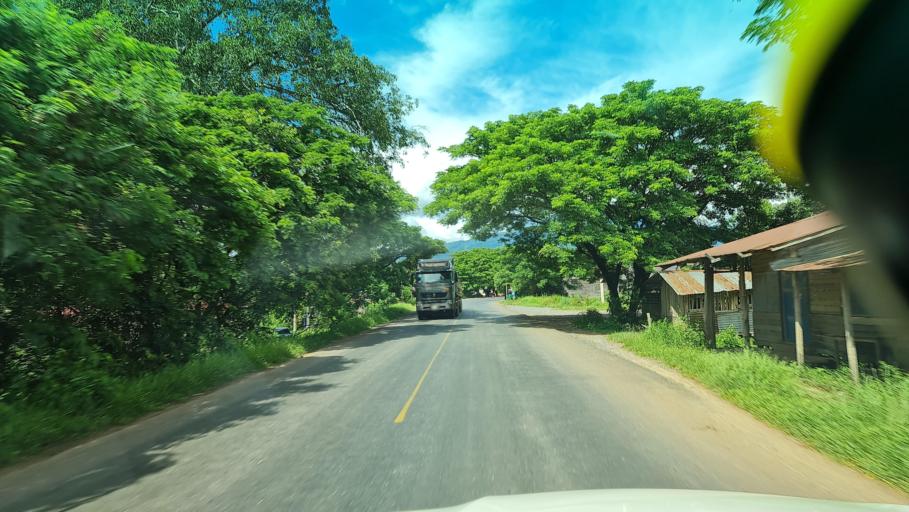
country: LA
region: Bolikhamxai
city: Pakkading
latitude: 18.2986
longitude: 104.0935
